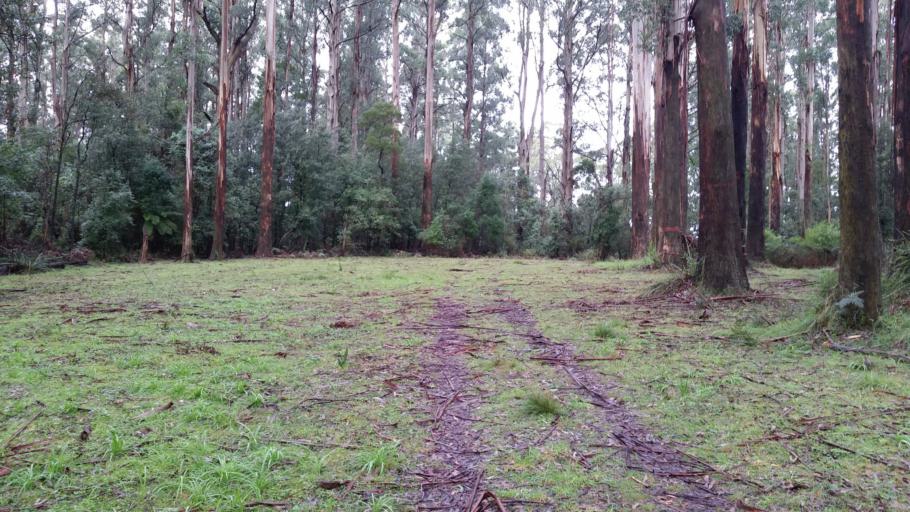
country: AU
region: Victoria
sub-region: Yarra Ranges
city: Belgrave
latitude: -37.8863
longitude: 145.3479
